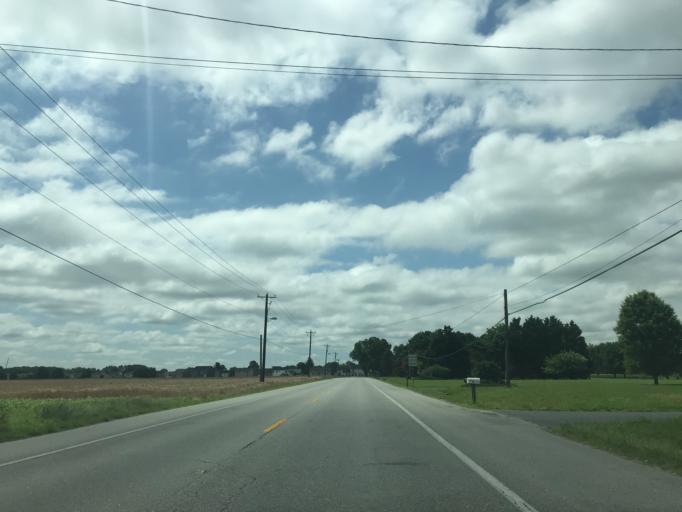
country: US
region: Maryland
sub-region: Caroline County
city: Ridgely
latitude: 38.9575
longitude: -75.8889
